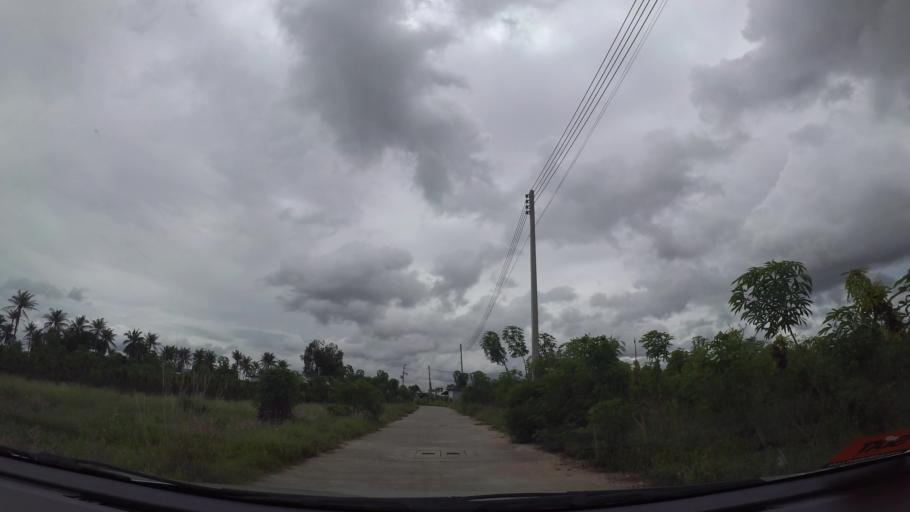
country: TH
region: Chon Buri
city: Si Racha
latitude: 13.1789
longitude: 100.9797
